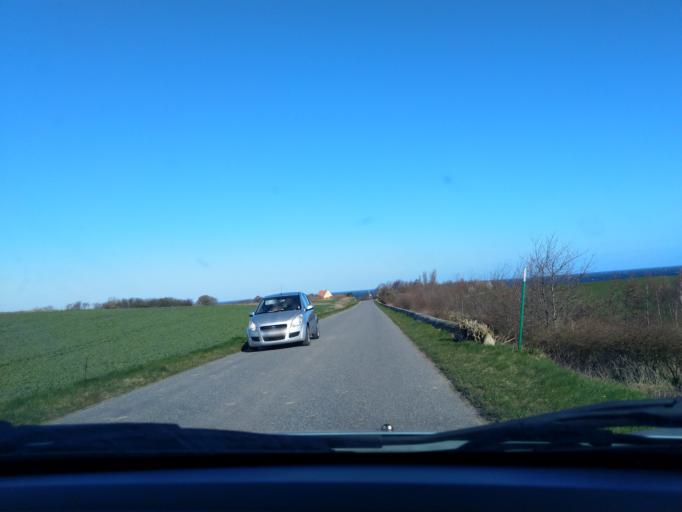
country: DK
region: Zealand
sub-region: Kalundborg Kommune
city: Kalundborg
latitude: 55.7448
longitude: 10.9510
